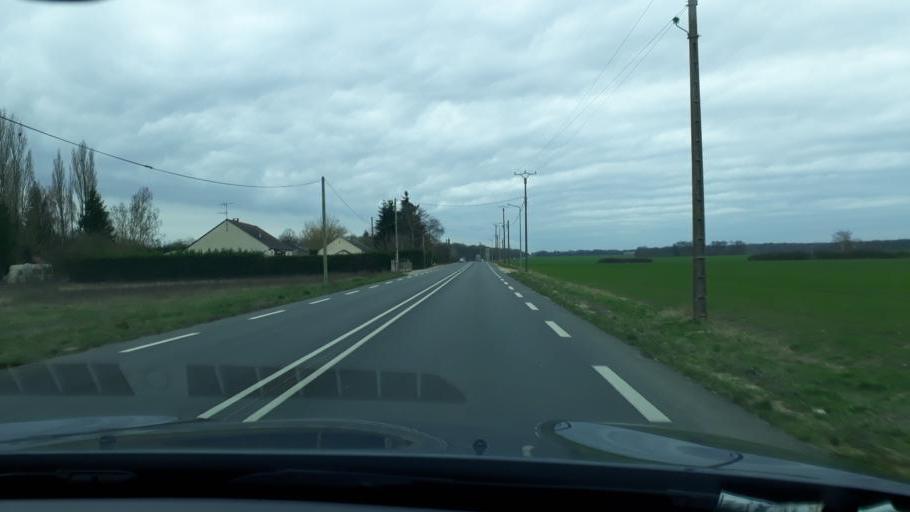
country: FR
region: Centre
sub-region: Departement du Loiret
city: Chanteau
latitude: 48.0310
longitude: 1.9735
